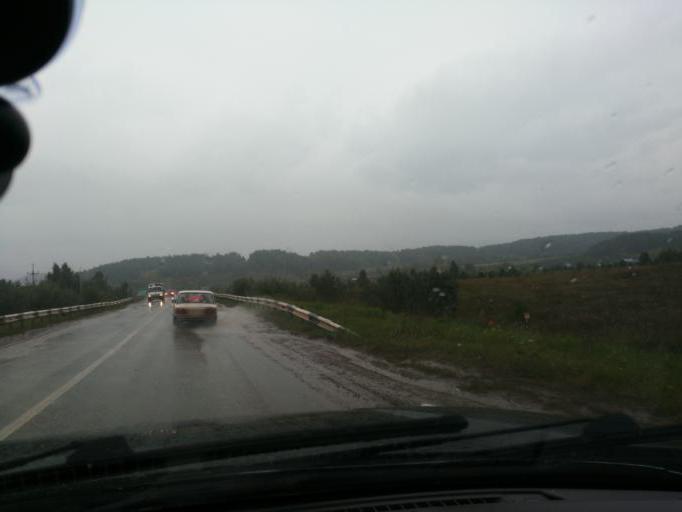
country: RU
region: Perm
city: Osa
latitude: 57.1957
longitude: 55.5918
